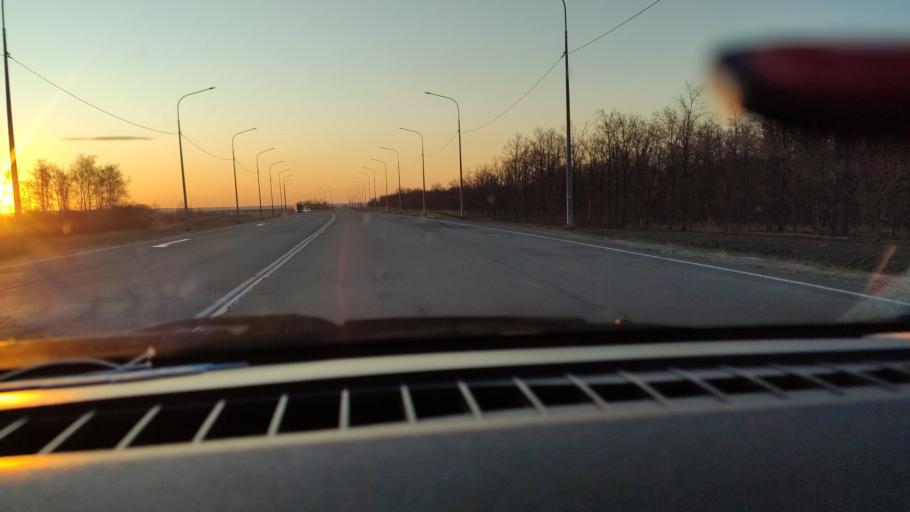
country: RU
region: Saratov
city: Yelshanka
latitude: 51.8198
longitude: 46.3533
